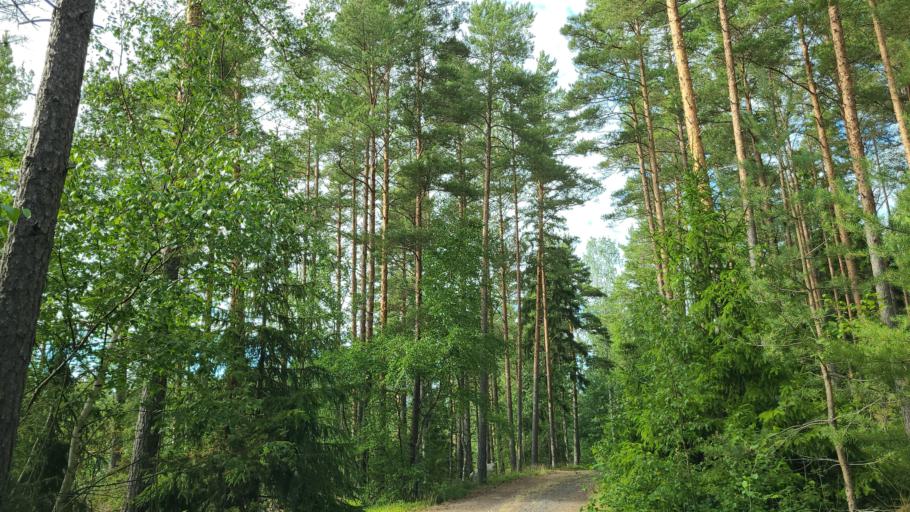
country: FI
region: Varsinais-Suomi
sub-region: Aboland-Turunmaa
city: Nagu
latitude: 60.2868
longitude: 21.9084
